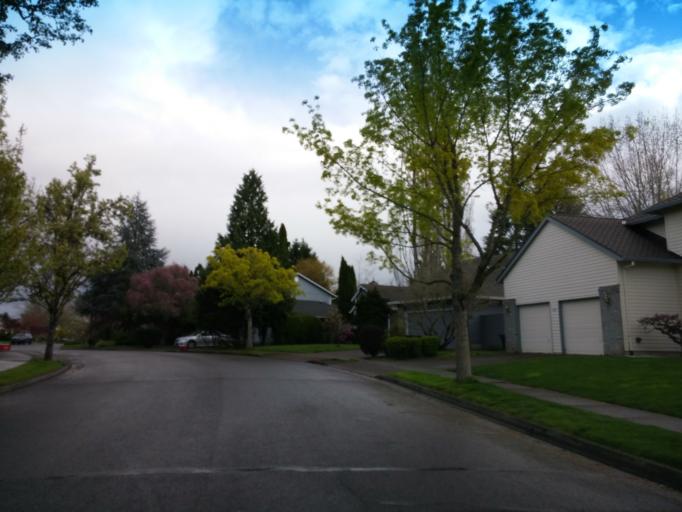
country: US
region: Oregon
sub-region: Washington County
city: Aloha
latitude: 45.5153
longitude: -122.8498
